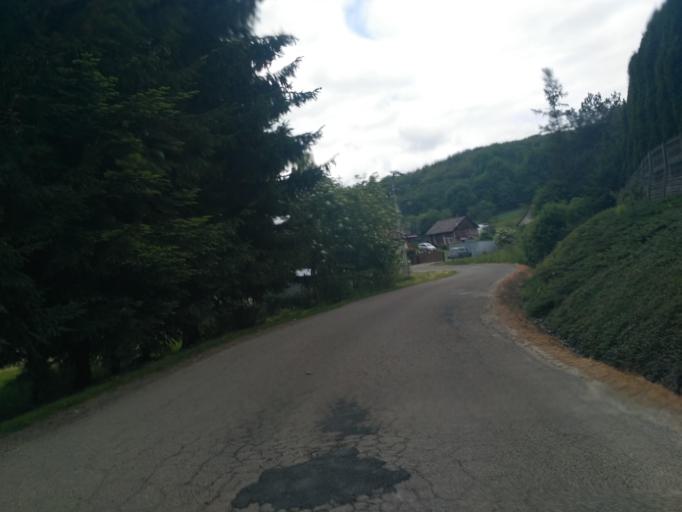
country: PL
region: Subcarpathian Voivodeship
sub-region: Powiat jasielski
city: Tarnowiec
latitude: 49.6904
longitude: 21.5954
